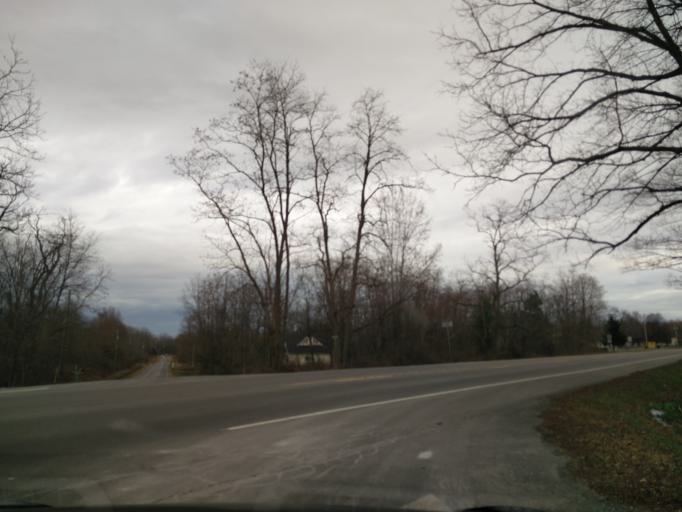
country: US
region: New York
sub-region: Tompkins County
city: Trumansburg
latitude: 42.5146
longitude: -76.6223
